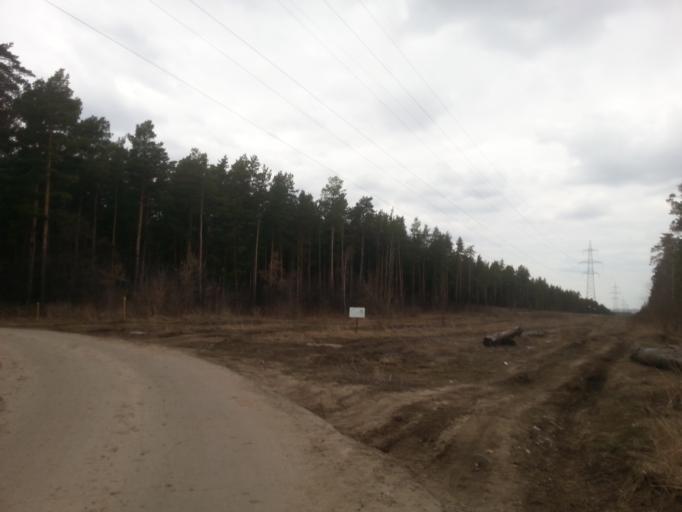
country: RU
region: Altai Krai
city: Yuzhnyy
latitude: 53.2892
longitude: 83.7281
